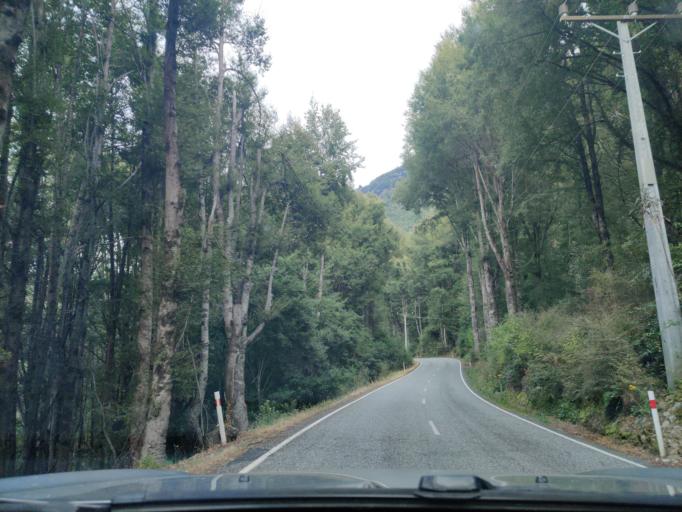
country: NZ
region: Otago
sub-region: Queenstown-Lakes District
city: Queenstown
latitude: -45.0702
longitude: 168.5042
